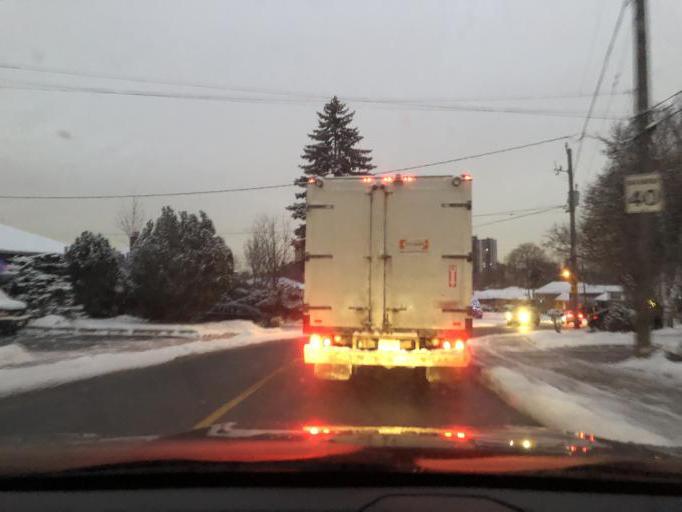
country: CA
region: Ontario
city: Toronto
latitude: 43.6986
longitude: -79.4805
